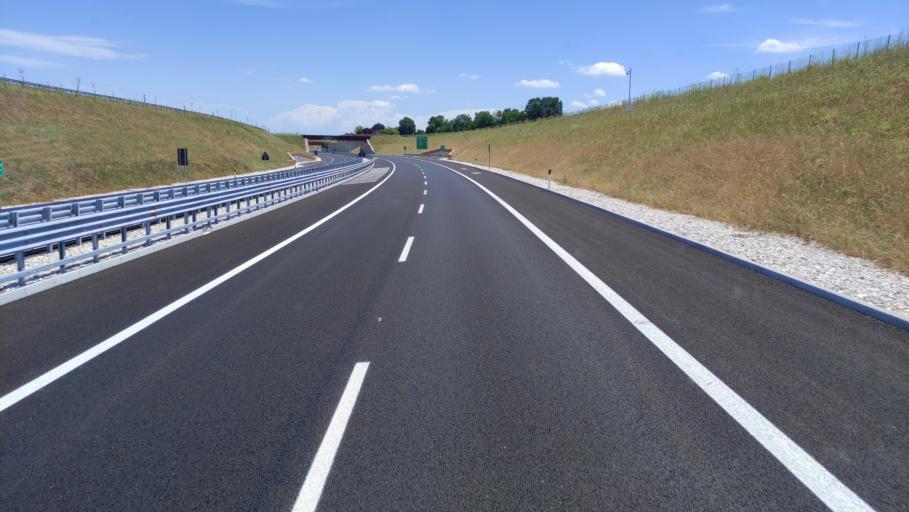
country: IT
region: Veneto
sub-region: Provincia di Treviso
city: Fanzolo
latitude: 45.7279
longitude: 11.9922
